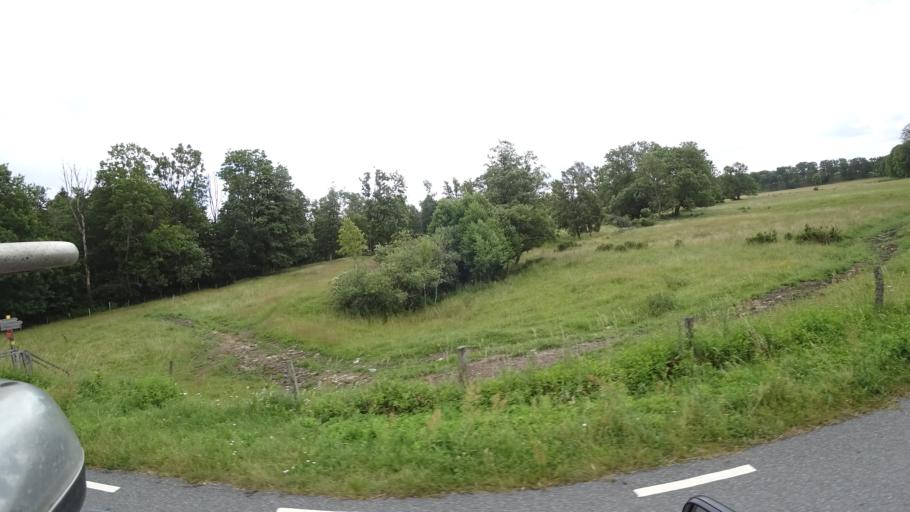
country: SE
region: Skane
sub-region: Kristianstads Kommun
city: Degeberga
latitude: 55.7141
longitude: 13.9846
